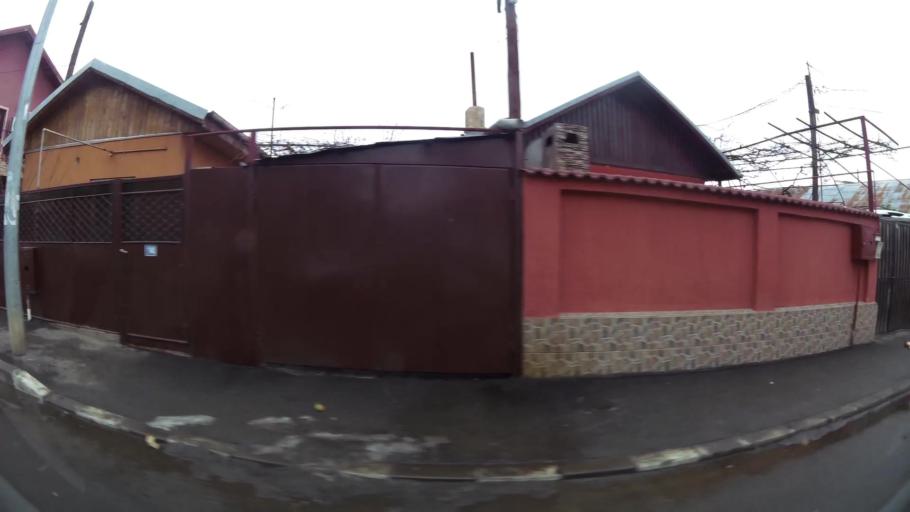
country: RO
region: Ilfov
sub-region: Comuna Pantelimon
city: Pantelimon
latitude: 44.4501
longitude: 26.1993
